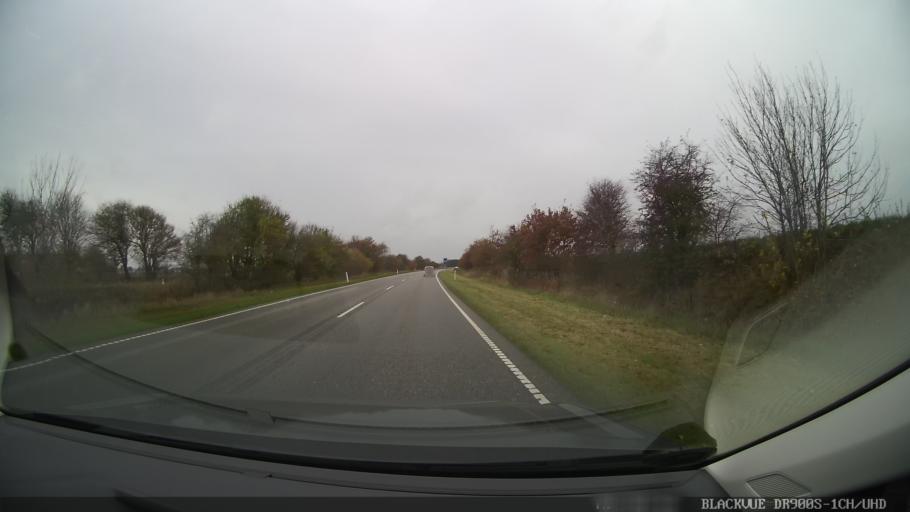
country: DK
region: North Denmark
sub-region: Thisted Kommune
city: Thisted
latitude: 56.8272
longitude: 8.7211
